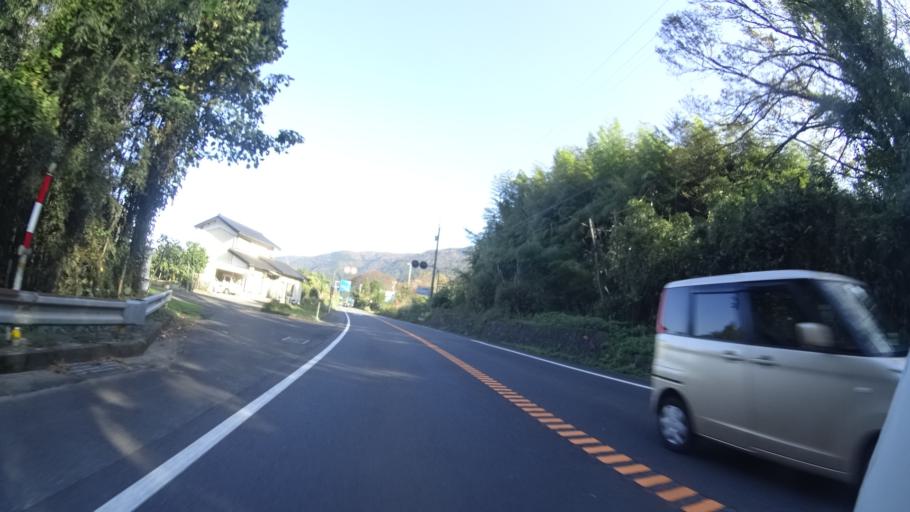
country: JP
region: Fukui
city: Tsuruga
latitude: 35.7385
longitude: 136.1007
